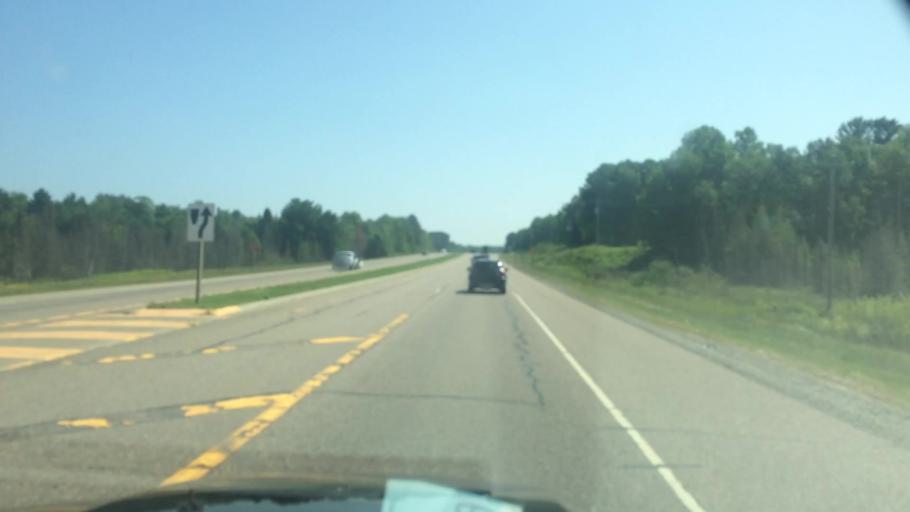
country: US
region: Wisconsin
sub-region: Oneida County
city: Rhinelander
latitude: 45.6177
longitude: -89.4905
